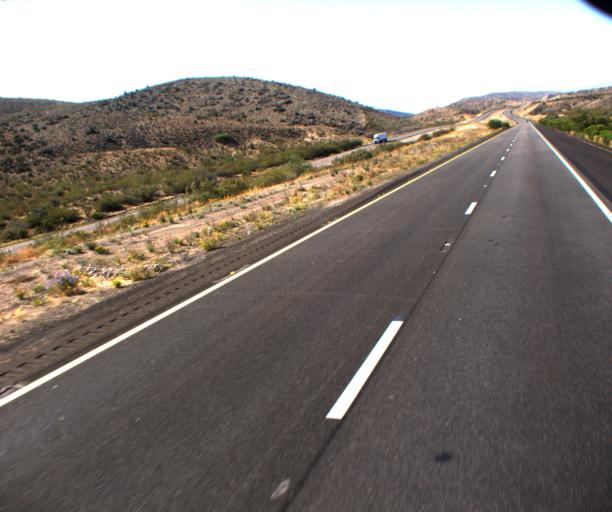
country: US
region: Arizona
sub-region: Mohave County
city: Kingman
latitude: 35.0238
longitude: -113.6648
